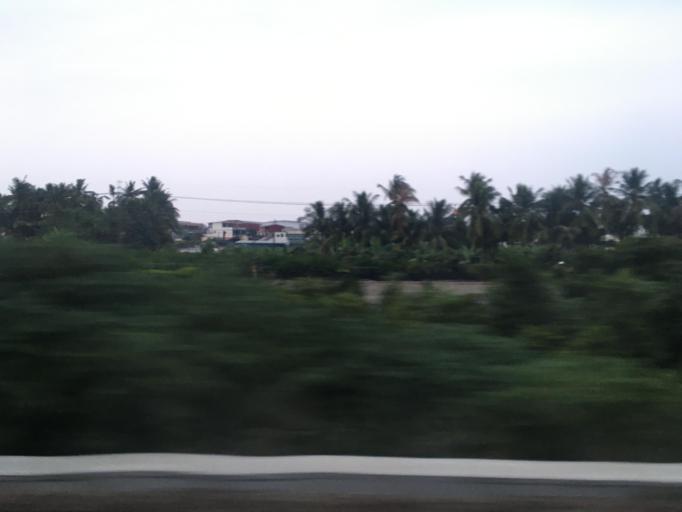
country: TW
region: Taiwan
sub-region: Pingtung
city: Pingtung
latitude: 22.6636
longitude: 120.4575
